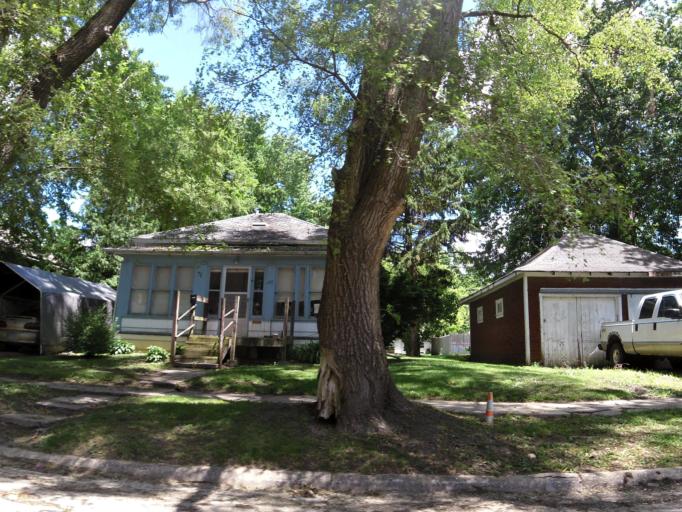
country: US
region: Iowa
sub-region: Fayette County
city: Oelwein
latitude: 42.6818
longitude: -91.9196
